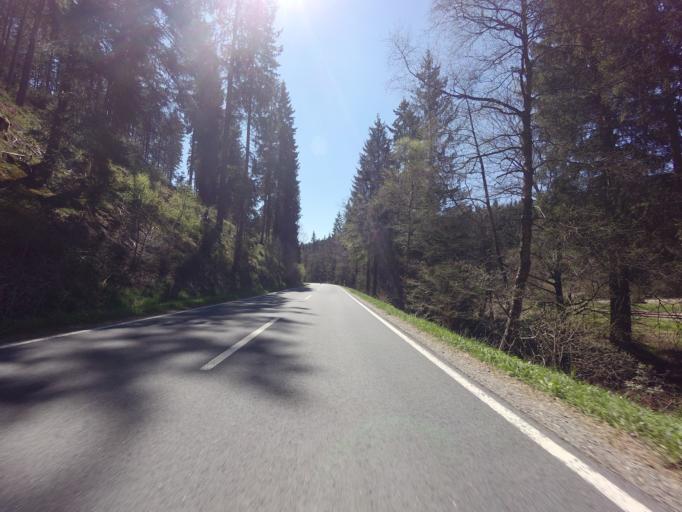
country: DE
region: North Rhine-Westphalia
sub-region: Regierungsbezirk Arnsberg
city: Erndtebruck
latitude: 51.0668
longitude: 8.2174
